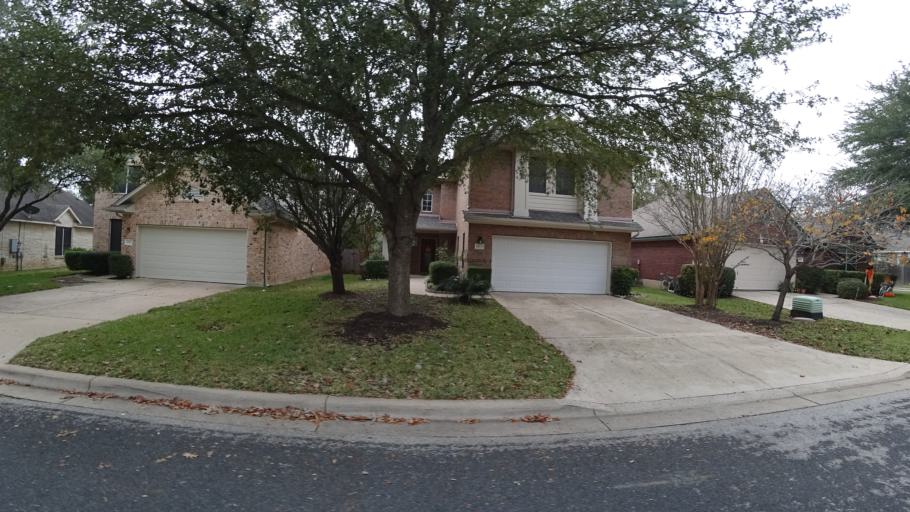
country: US
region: Texas
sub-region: Travis County
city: Barton Creek
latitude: 30.2255
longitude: -97.8785
